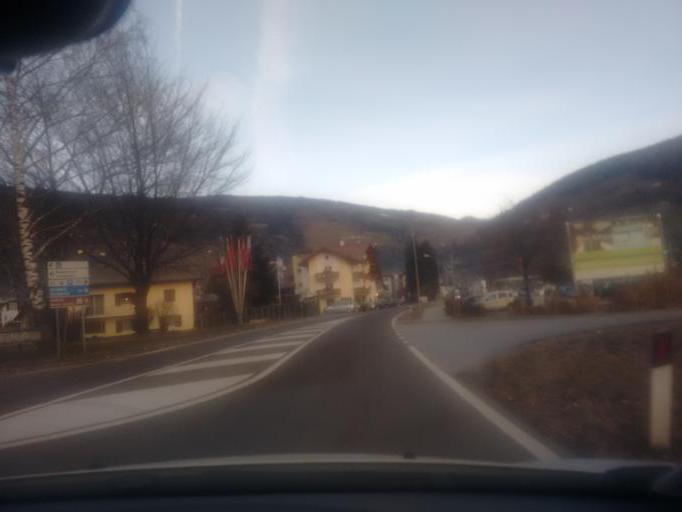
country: IT
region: Trentino-Alto Adige
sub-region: Bolzano
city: Vipiteno
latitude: 46.8921
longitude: 11.4359
